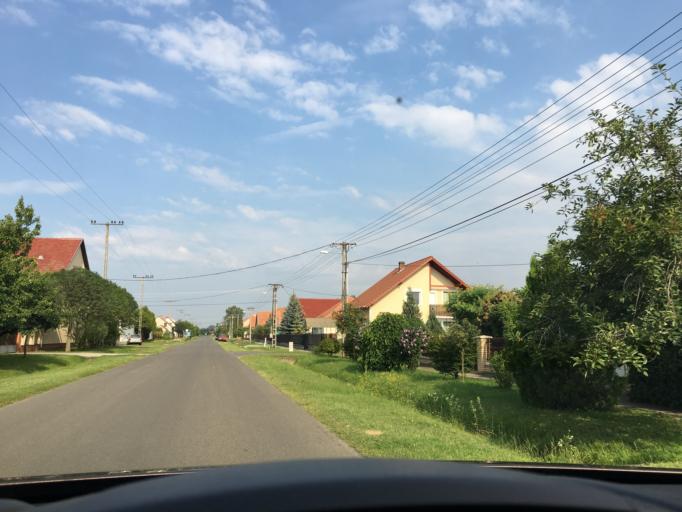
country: HU
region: Csongrad
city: Morahalom
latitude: 46.2103
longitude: 19.8839
